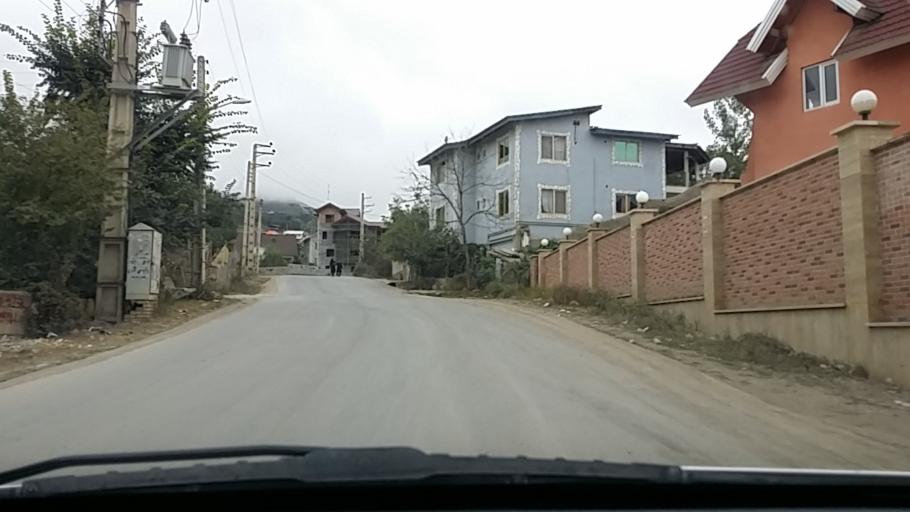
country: IR
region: Mazandaran
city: `Abbasabad
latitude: 36.5004
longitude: 51.1577
